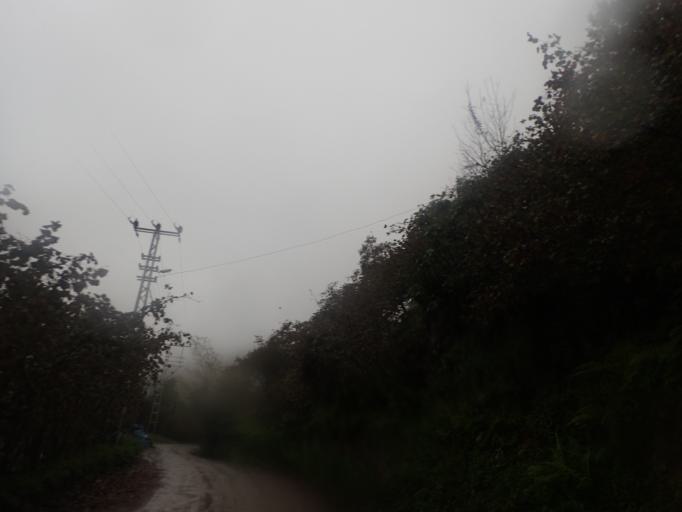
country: TR
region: Ordu
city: Persembe
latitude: 41.0389
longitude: 37.7213
